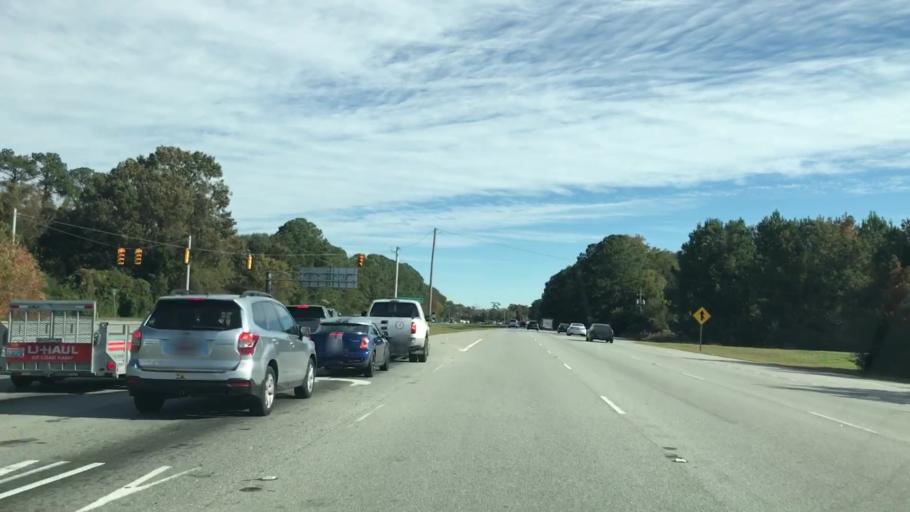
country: US
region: South Carolina
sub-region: Charleston County
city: Shell Point
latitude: 32.8093
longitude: -80.0360
